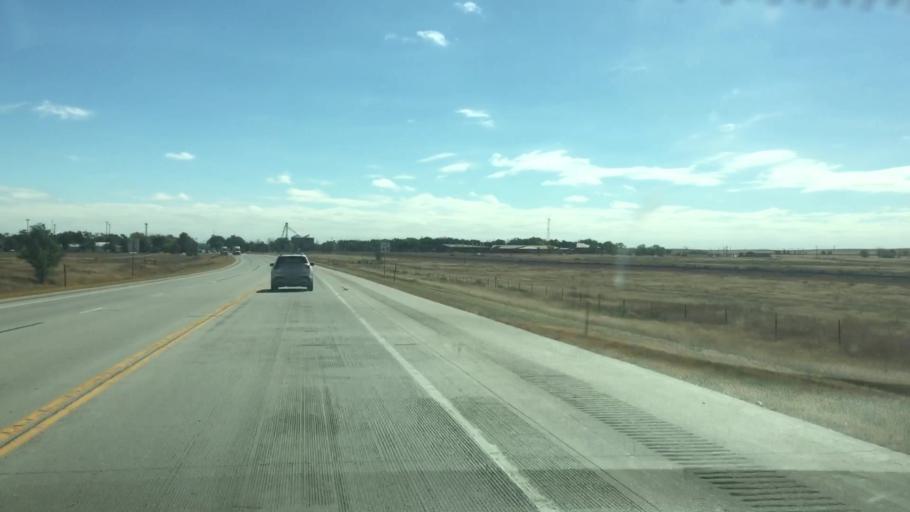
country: US
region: Colorado
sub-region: Lincoln County
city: Hugo
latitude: 39.1386
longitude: -103.4818
